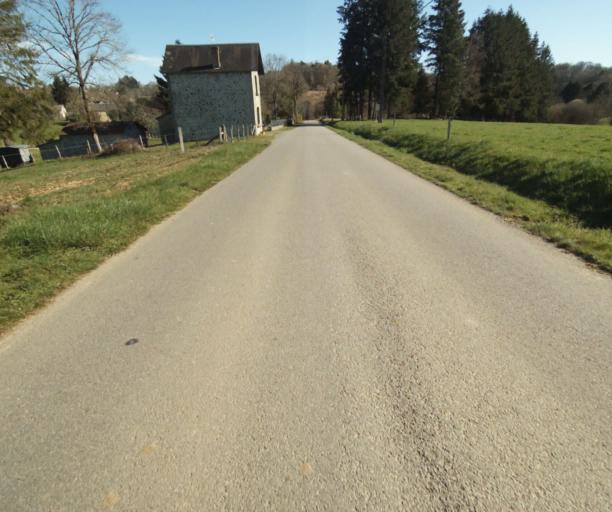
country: FR
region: Limousin
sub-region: Departement de la Correze
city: Chamboulive
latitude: 45.4716
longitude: 1.7213
